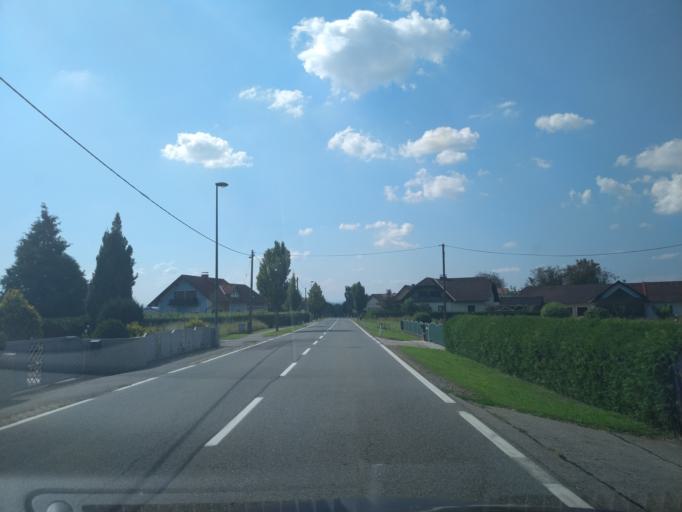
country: AT
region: Styria
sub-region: Politischer Bezirk Leibnitz
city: Obervogau
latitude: 46.7580
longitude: 15.6004
